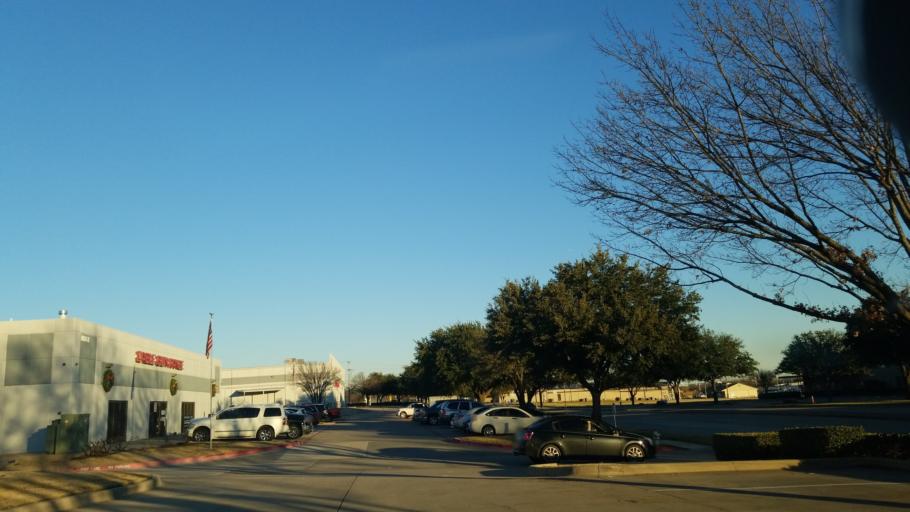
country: US
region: Texas
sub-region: Denton County
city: Lewisville
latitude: 33.0580
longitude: -97.0038
